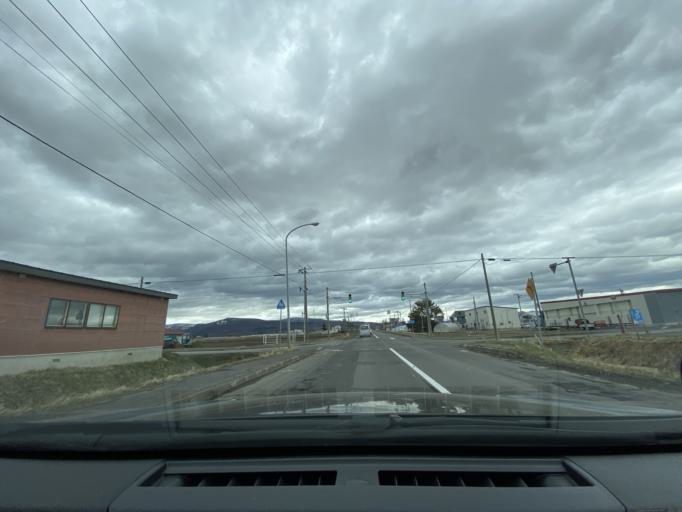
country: JP
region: Hokkaido
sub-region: Asahikawa-shi
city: Asahikawa
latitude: 43.8759
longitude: 142.4853
